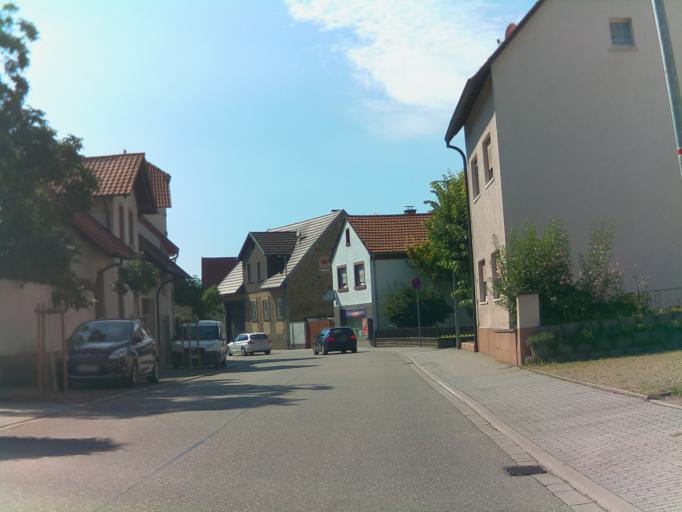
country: DE
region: Baden-Wuerttemberg
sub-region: Karlsruhe Region
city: Ubstadt-Weiher
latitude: 49.1787
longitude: 8.6781
